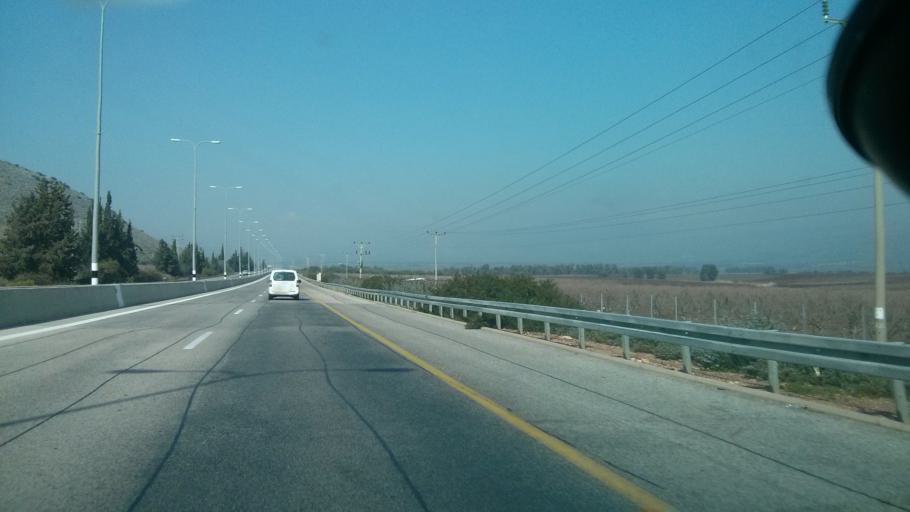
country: IL
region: Northern District
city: Rosh Pinna
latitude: 33.0596
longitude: 35.5743
